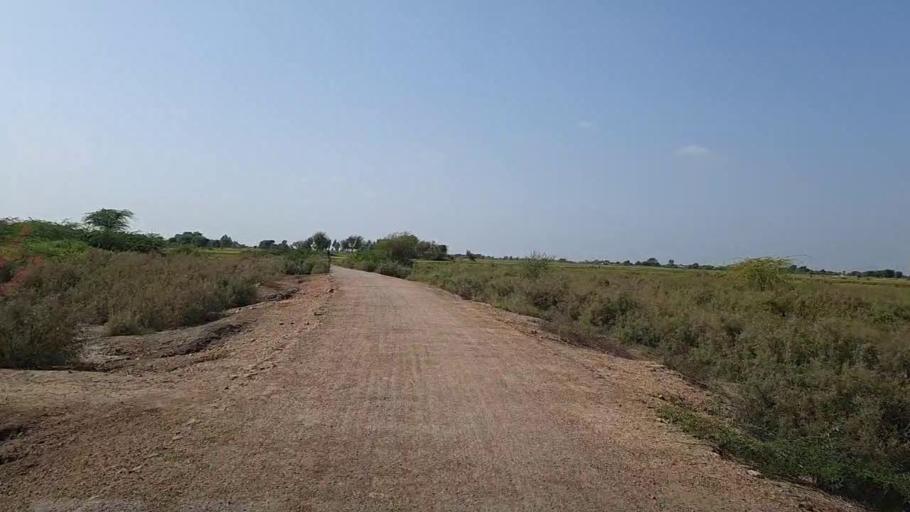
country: PK
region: Sindh
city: Kario
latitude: 24.7887
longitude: 68.5395
